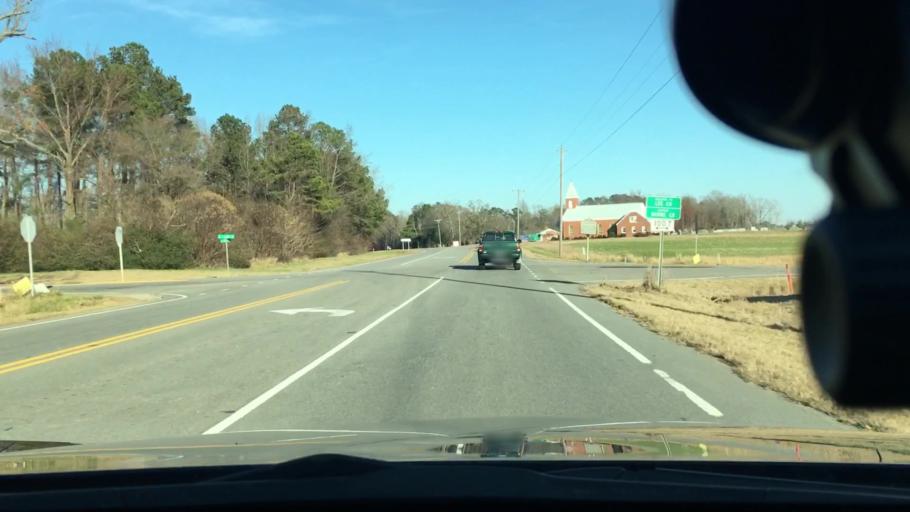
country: US
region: North Carolina
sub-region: Lee County
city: Sanford
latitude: 35.3813
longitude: -79.2807
